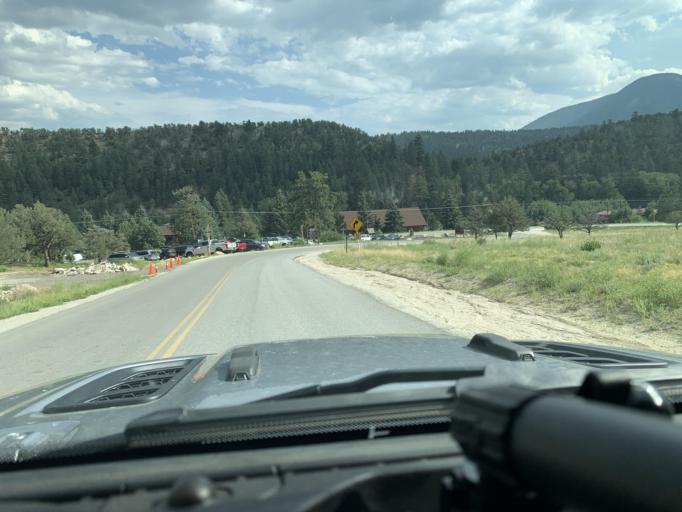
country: US
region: Colorado
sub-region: Chaffee County
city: Buena Vista
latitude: 38.7341
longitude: -106.1641
